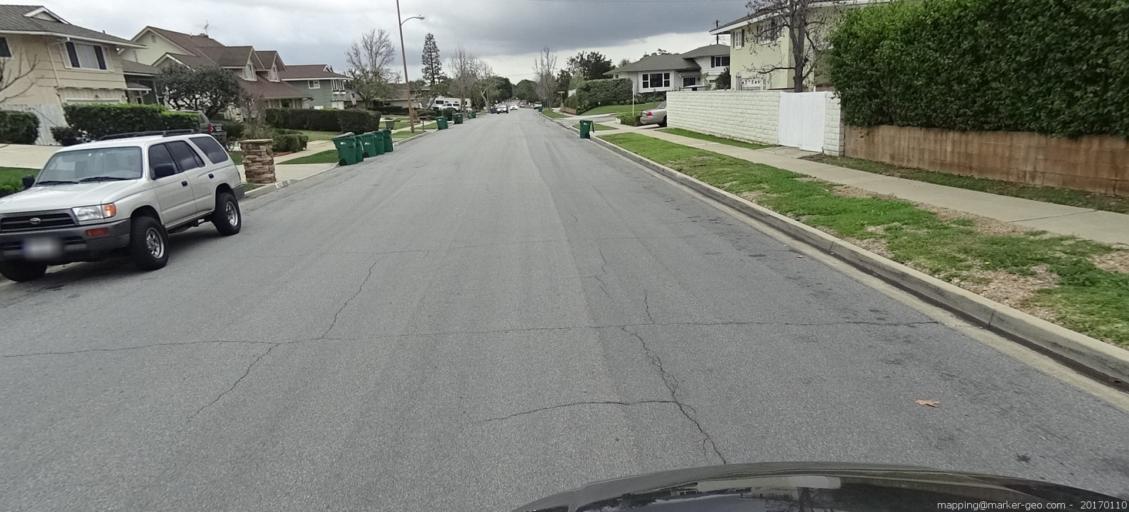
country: US
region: California
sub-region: Orange County
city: Tustin
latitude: 33.7701
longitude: -117.8254
